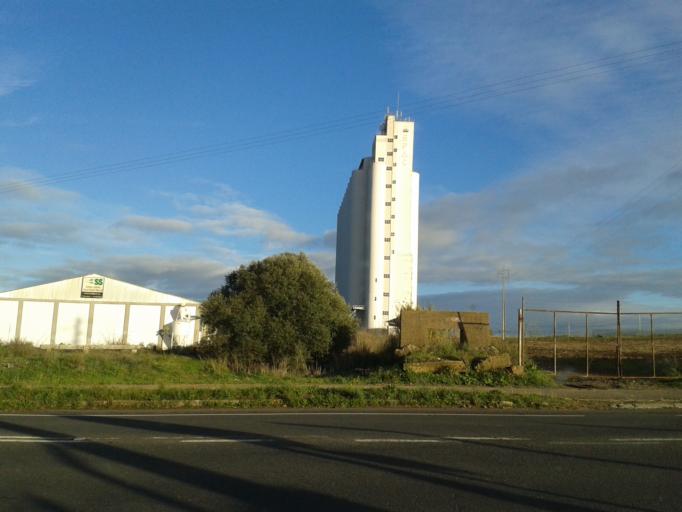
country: PT
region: Beja
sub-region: Beja
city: Beja
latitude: 38.0325
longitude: -7.8731
